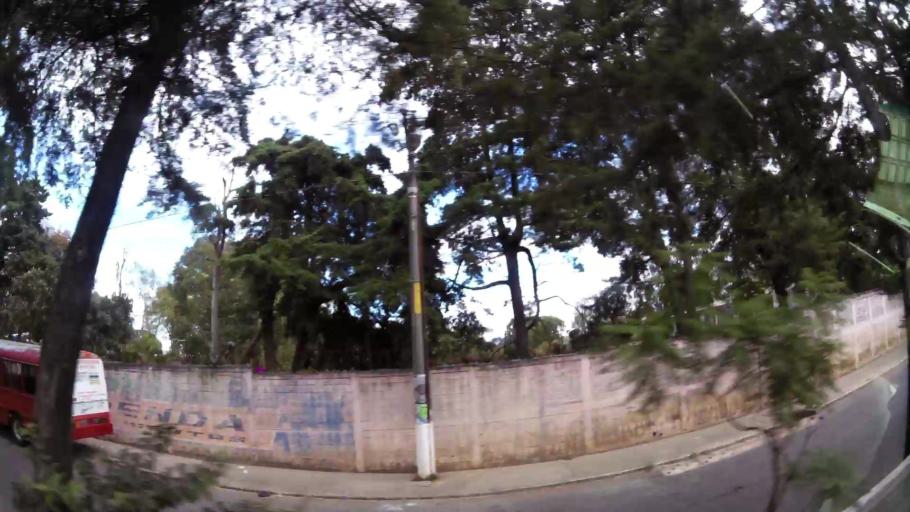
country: GT
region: Guatemala
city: Mixco
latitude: 14.6710
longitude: -90.5677
